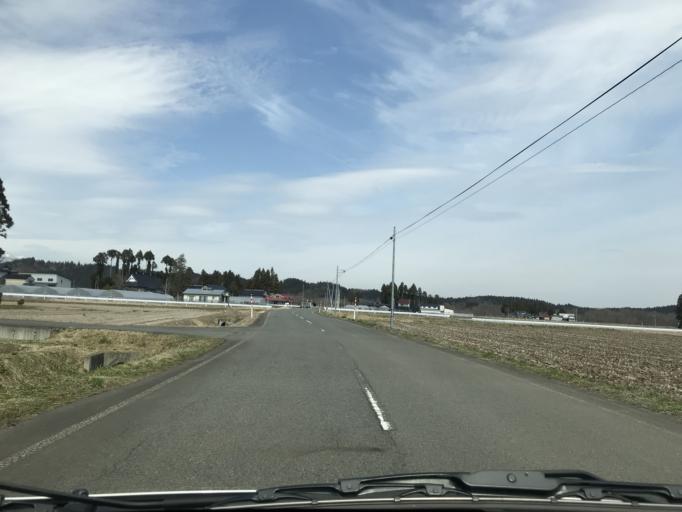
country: JP
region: Iwate
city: Mizusawa
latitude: 39.1429
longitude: 141.0579
